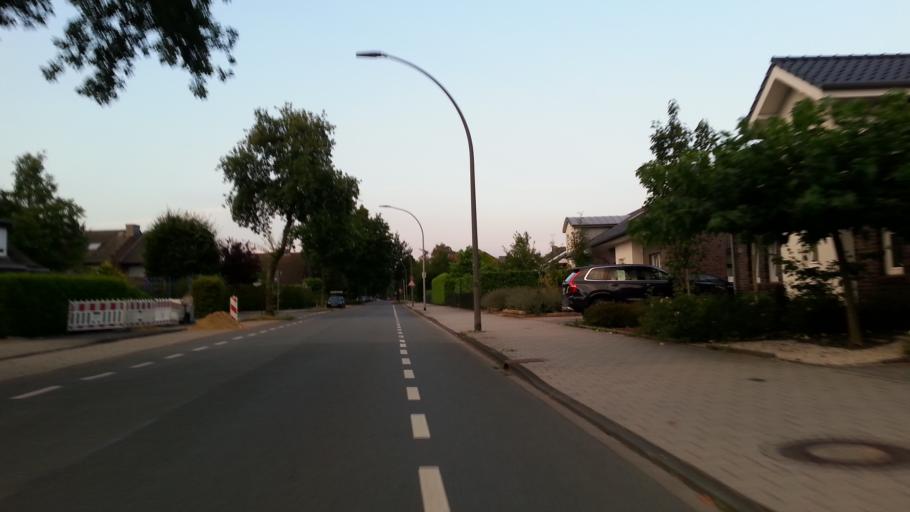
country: DE
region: North Rhine-Westphalia
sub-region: Regierungsbezirk Munster
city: Muenster
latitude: 51.9482
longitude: 7.5393
